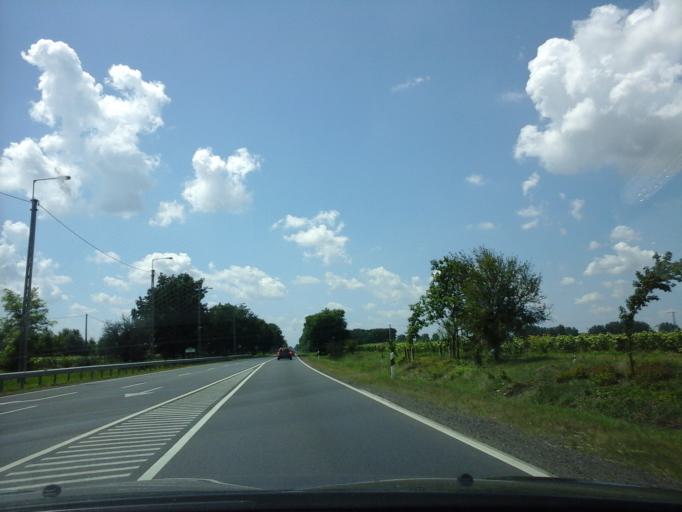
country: HU
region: Hajdu-Bihar
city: Ebes
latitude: 47.4815
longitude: 21.4998
